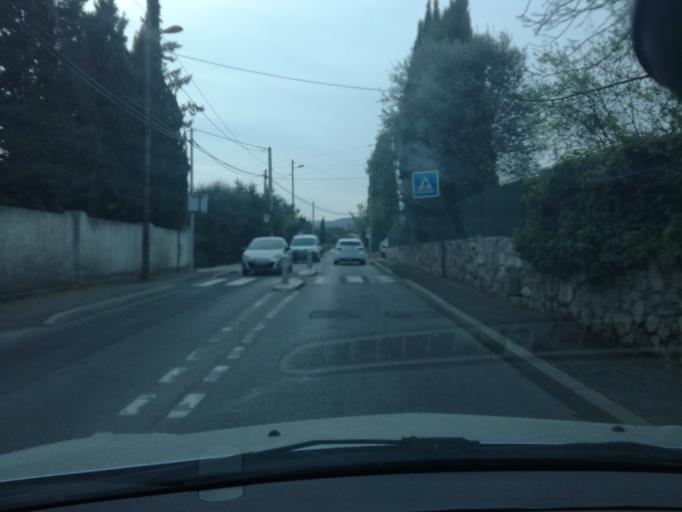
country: FR
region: Provence-Alpes-Cote d'Azur
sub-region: Departement des Alpes-Maritimes
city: Grasse
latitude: 43.6389
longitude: 6.9217
